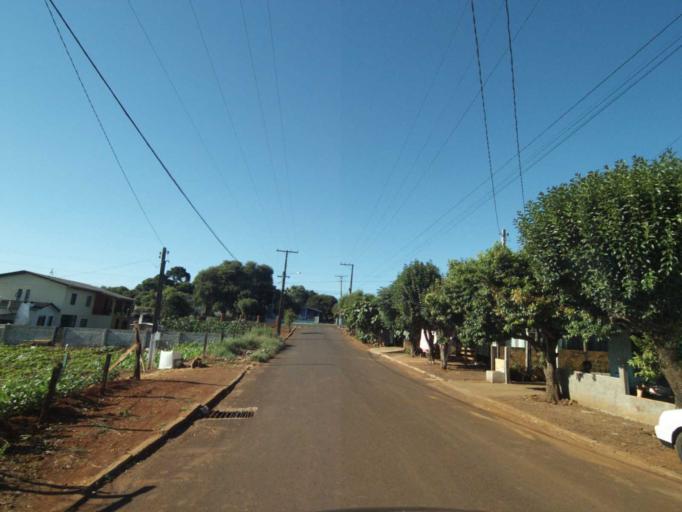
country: BR
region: Parana
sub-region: Coronel Vivida
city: Coronel Vivida
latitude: -25.9597
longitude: -52.8120
